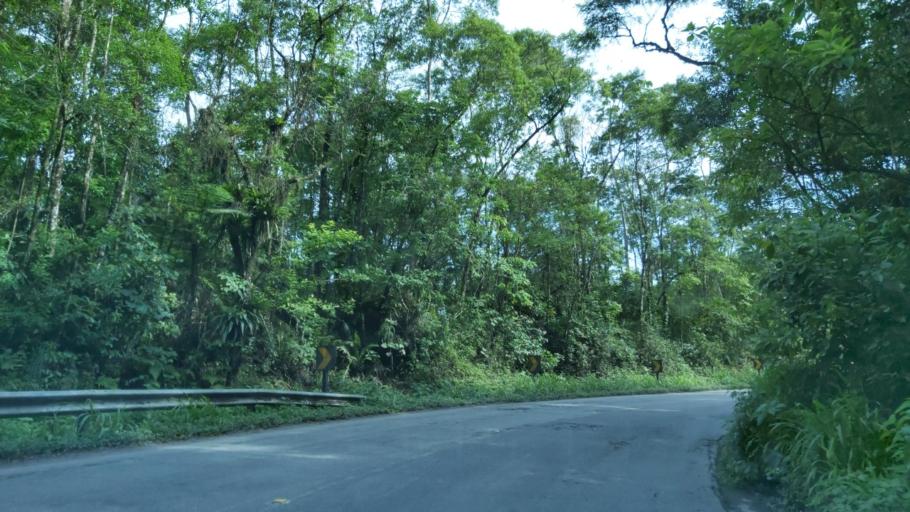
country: BR
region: Sao Paulo
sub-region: Miracatu
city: Miracatu
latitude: -24.0409
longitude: -47.5680
